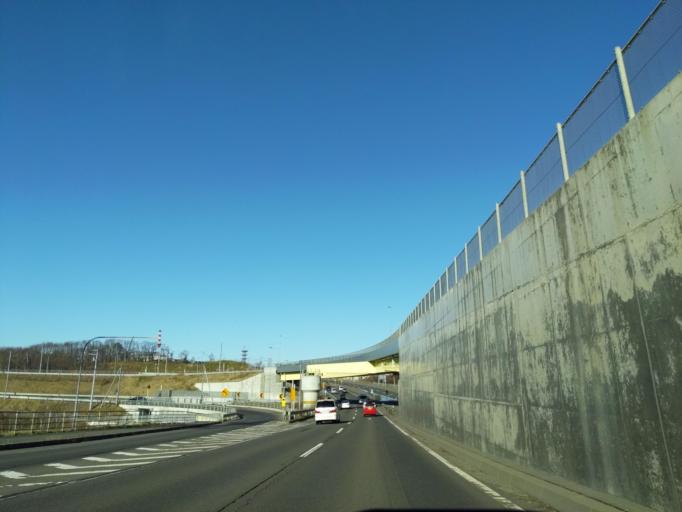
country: JP
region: Hokkaido
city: Kitahiroshima
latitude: 42.9547
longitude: 141.4959
